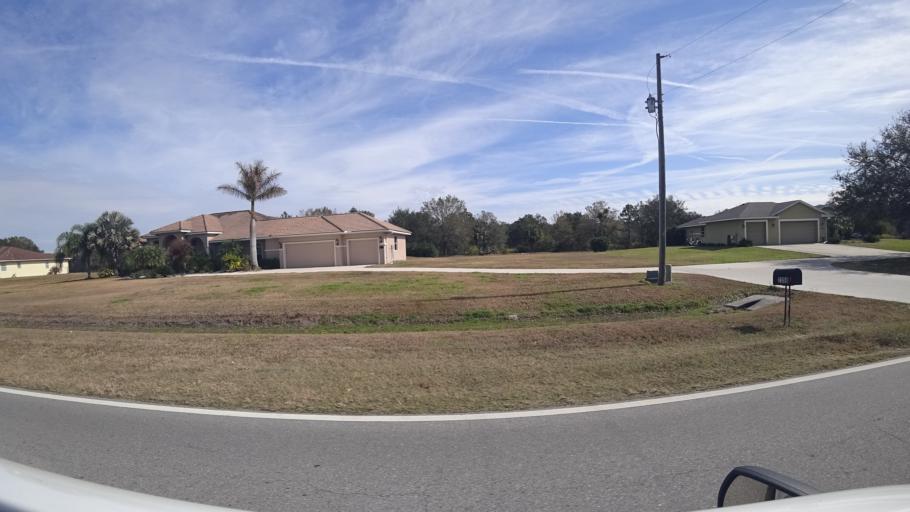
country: US
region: Florida
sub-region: Manatee County
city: Ellenton
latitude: 27.5326
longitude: -82.3687
